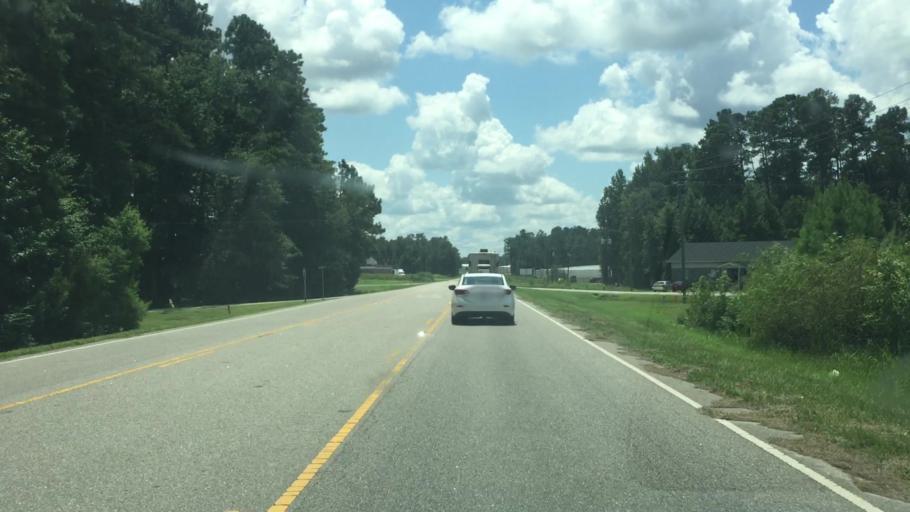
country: US
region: North Carolina
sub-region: Columbus County
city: Tabor City
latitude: 34.1538
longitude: -78.8597
